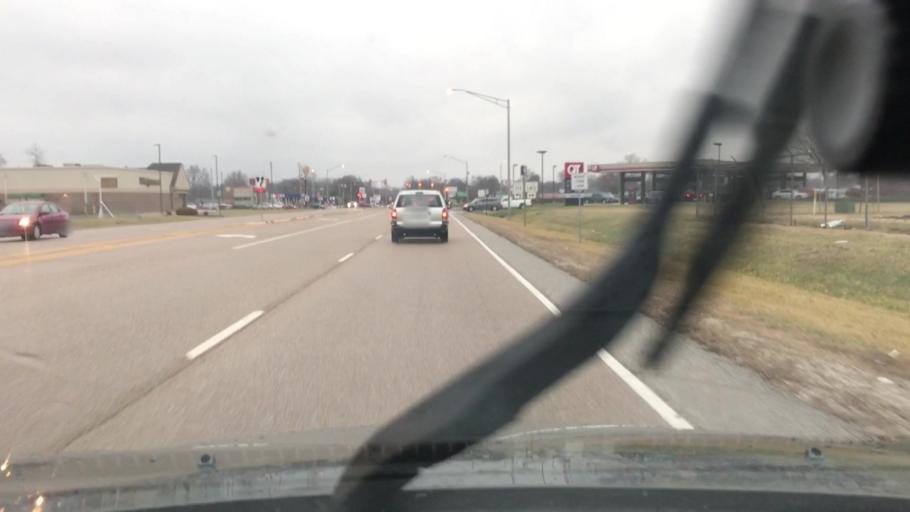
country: US
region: Illinois
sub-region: Madison County
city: Bethalto
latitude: 38.8990
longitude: -90.0592
